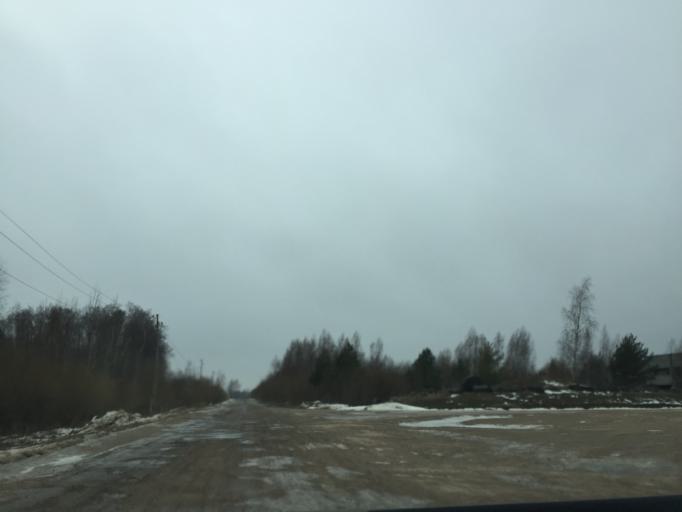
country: LV
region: Lecava
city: Iecava
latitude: 56.5751
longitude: 24.0689
